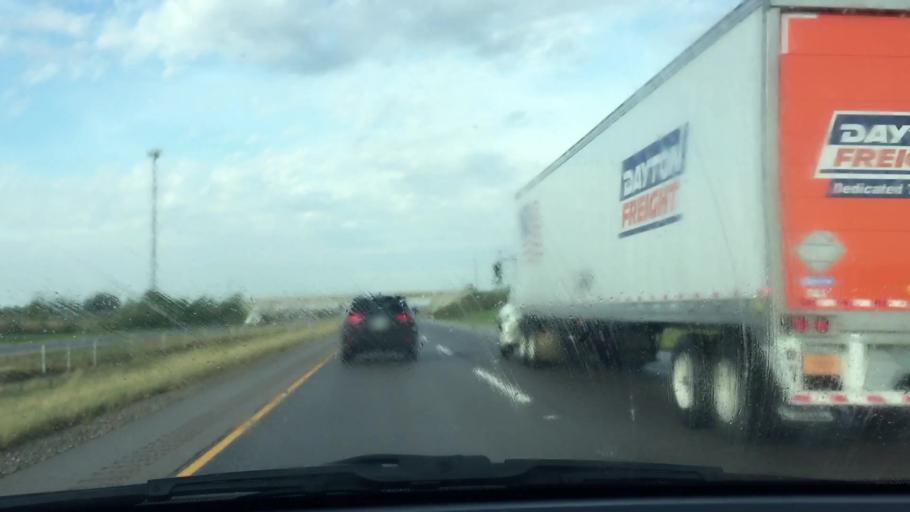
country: US
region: Illinois
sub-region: Lee County
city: Franklin Grove
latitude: 41.8229
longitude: -89.3389
